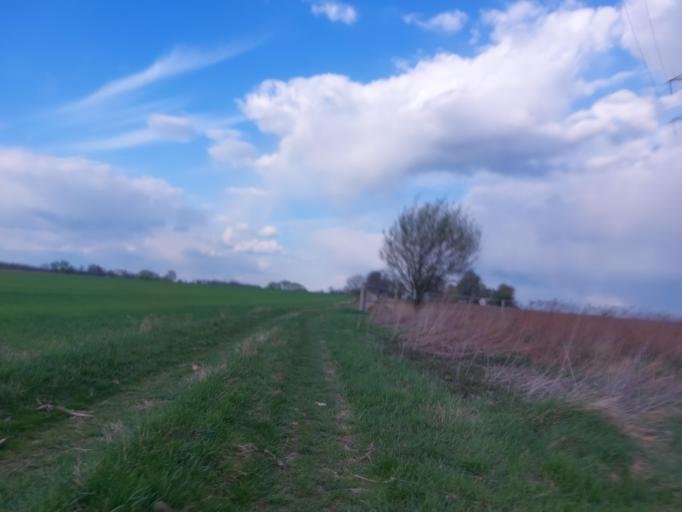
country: HU
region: Veszprem
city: Devecser
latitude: 47.1515
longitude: 17.4052
